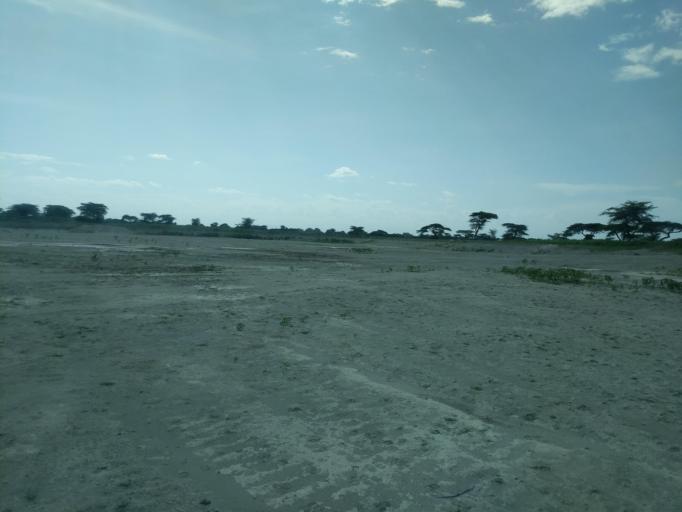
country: ET
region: Oromiya
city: Ziway
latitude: 7.6916
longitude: 38.6474
